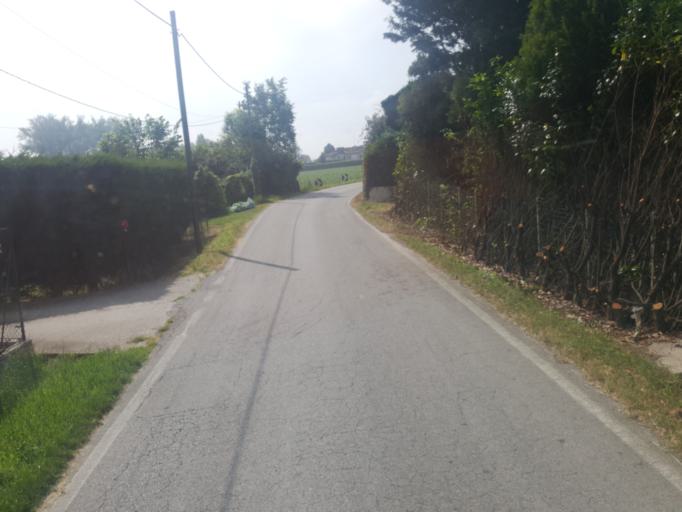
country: IT
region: Veneto
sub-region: Provincia di Rovigo
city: Canaro
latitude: 44.9367
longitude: 11.6497
